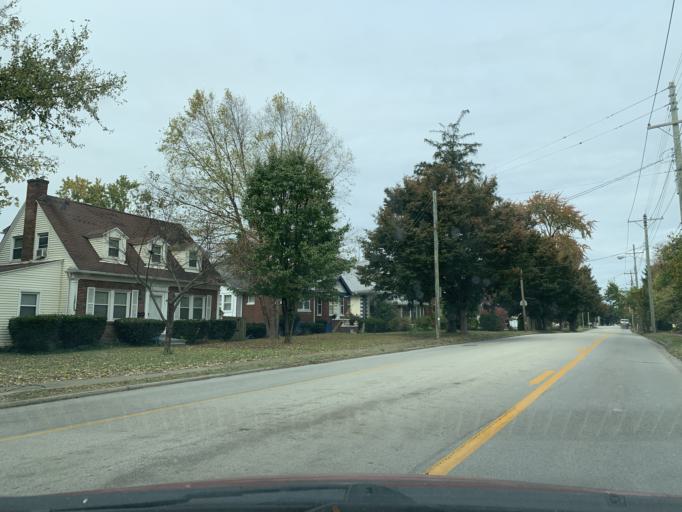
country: US
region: Kentucky
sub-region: Jefferson County
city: Audubon Park
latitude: 38.1789
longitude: -85.7667
